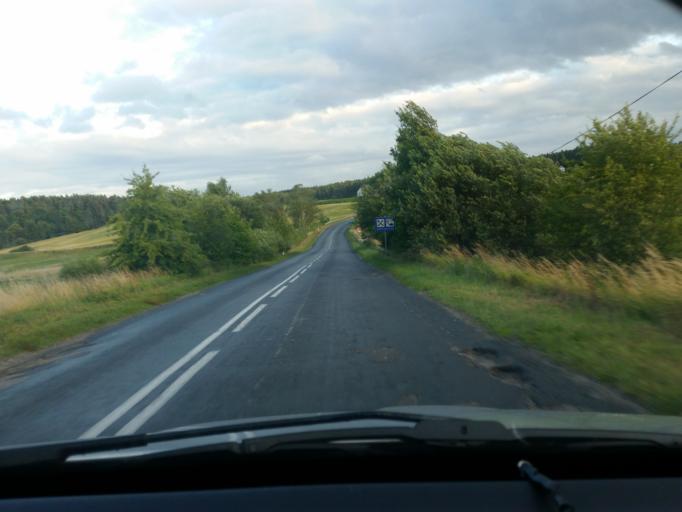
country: PL
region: Pomeranian Voivodeship
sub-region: Powiat czluchowski
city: Czluchow
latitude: 53.8165
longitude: 17.4096
